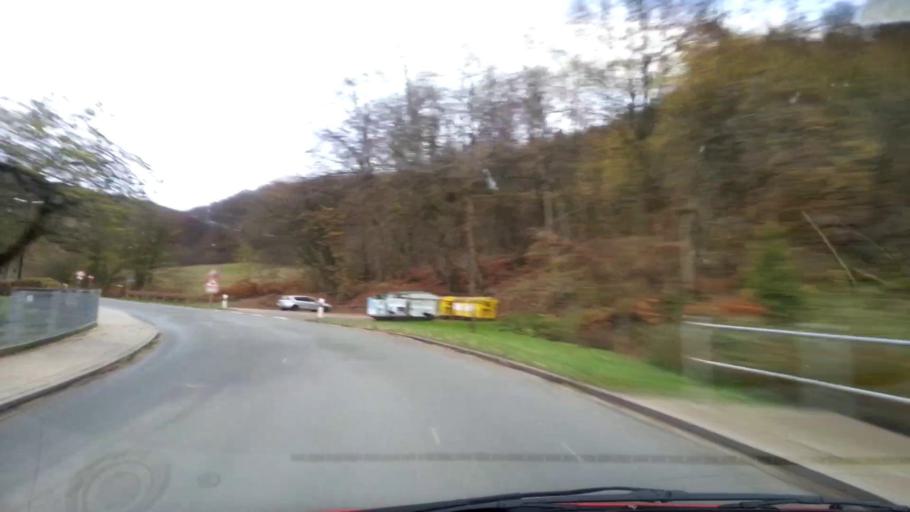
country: DE
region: Bavaria
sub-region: Upper Franconia
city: Poxdorf
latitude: 49.9174
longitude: 11.0766
